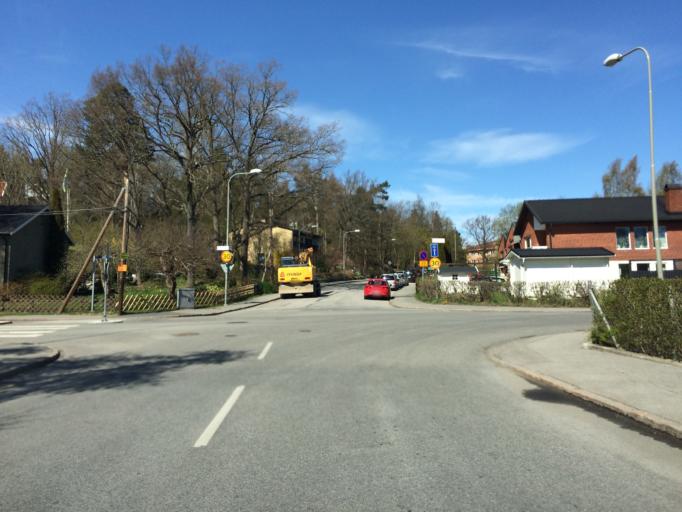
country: SE
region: Stockholm
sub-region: Huddinge Kommun
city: Segeltorp
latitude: 59.2797
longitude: 17.9610
